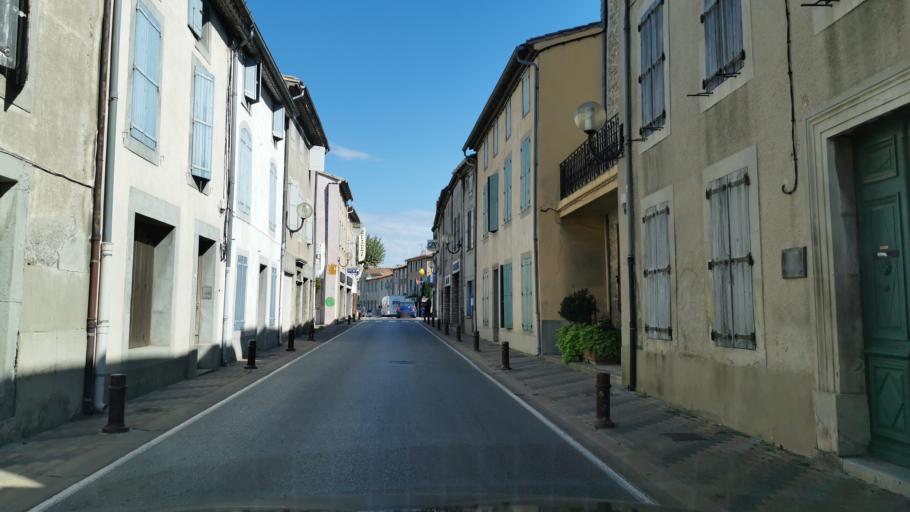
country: FR
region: Languedoc-Roussillon
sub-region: Departement de l'Aude
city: Rieux-Minervois
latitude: 43.2823
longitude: 2.5859
